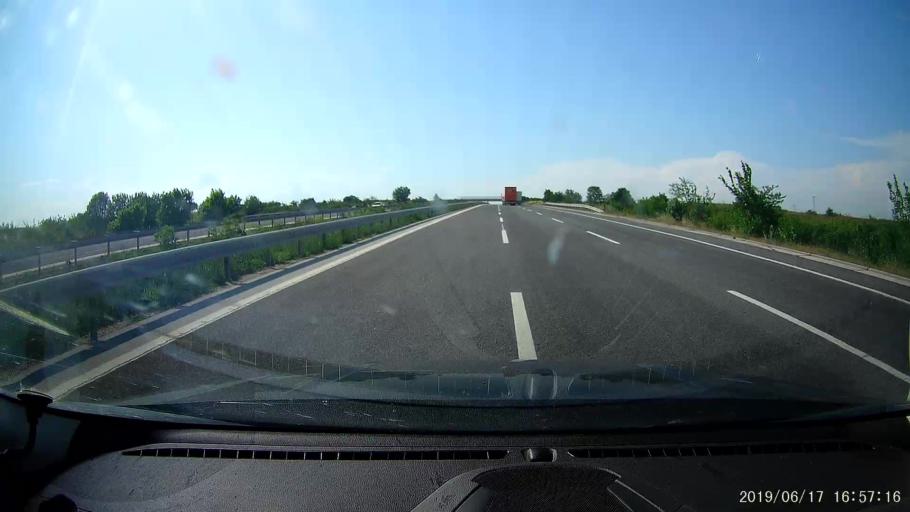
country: TR
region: Edirne
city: Haskoy
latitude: 41.5981
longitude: 26.9180
